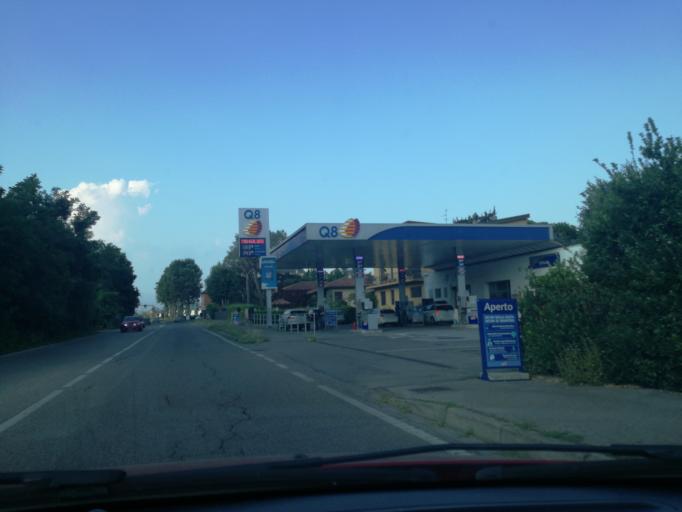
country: IT
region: Lombardy
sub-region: Provincia di Monza e Brianza
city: Arcore
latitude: 45.6337
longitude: 9.3349
